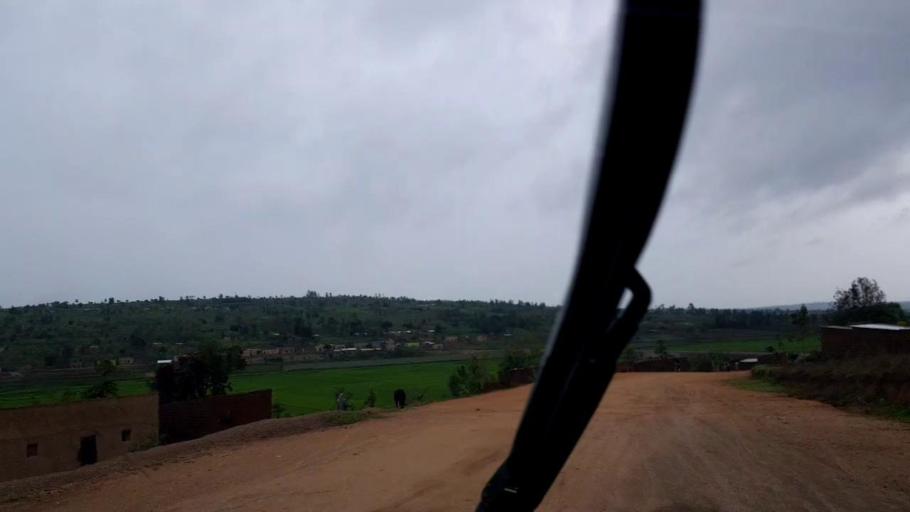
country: RW
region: Northern Province
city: Byumba
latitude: -1.4248
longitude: 30.2721
